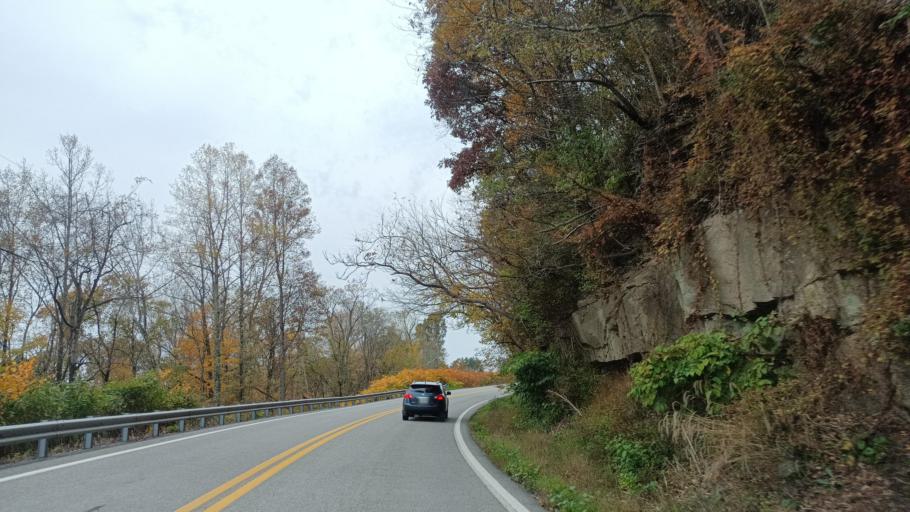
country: US
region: West Virginia
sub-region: Taylor County
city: Grafton
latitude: 39.3423
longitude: -79.9585
